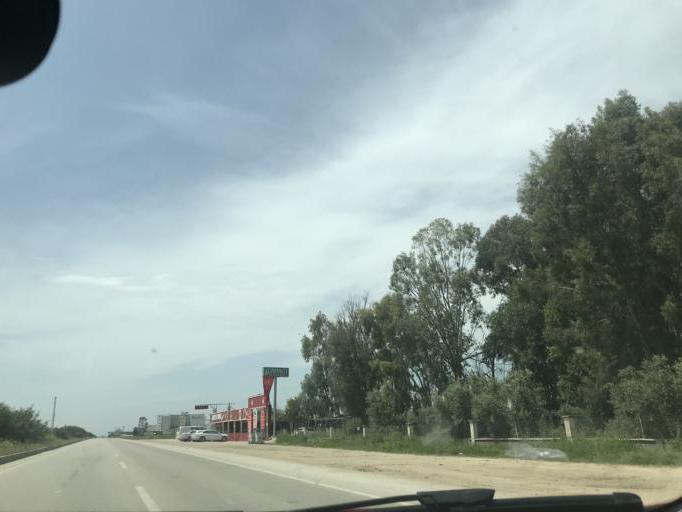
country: TR
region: Adana
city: Yakapinar
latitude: 36.9735
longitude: 35.5047
